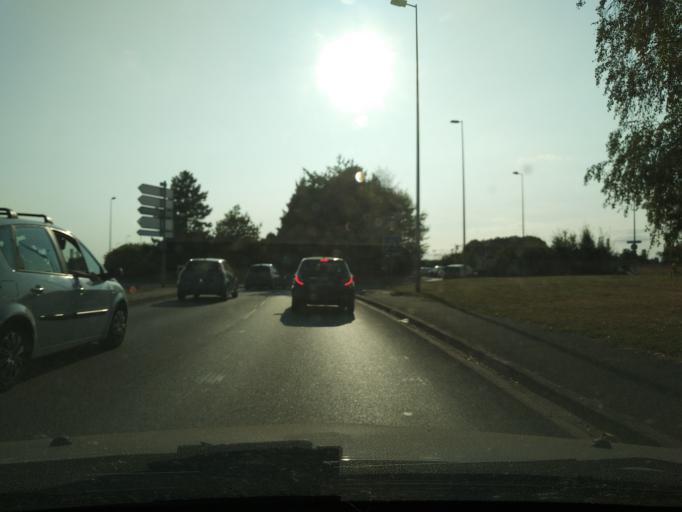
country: FR
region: Centre
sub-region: Departement d'Indre-et-Loire
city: Mettray
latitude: 47.4285
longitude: 0.6610
